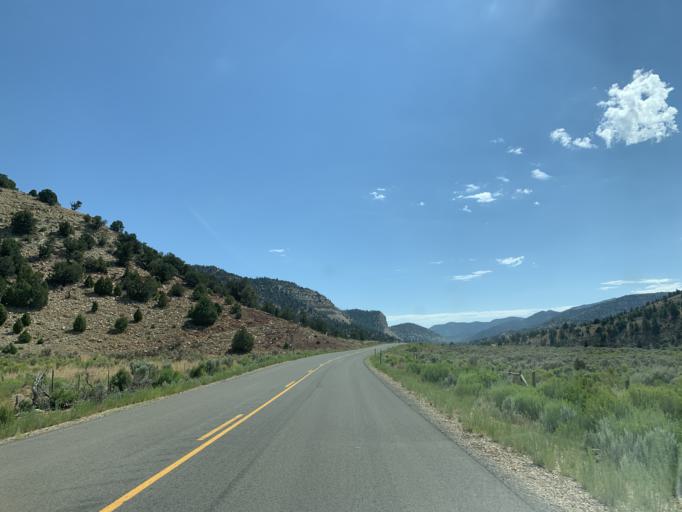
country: US
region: Utah
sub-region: Carbon County
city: East Carbon City
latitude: 39.7758
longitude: -110.5061
